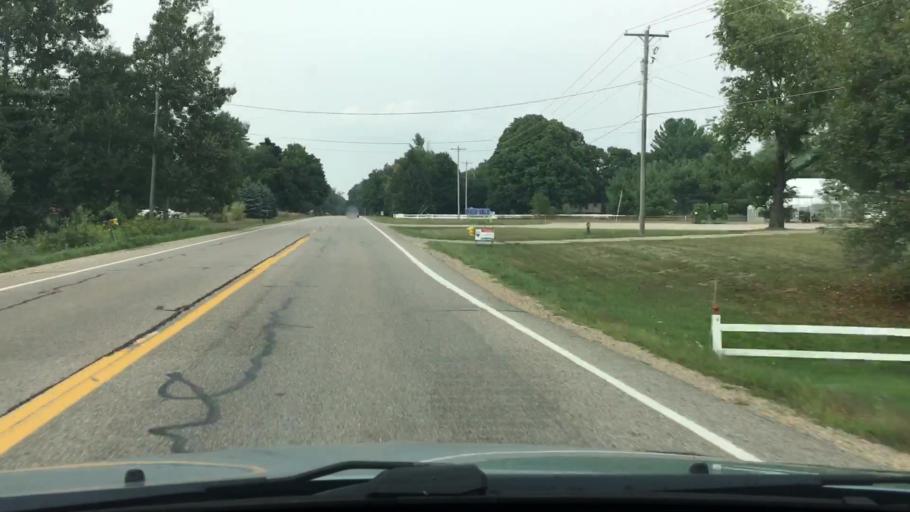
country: US
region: Michigan
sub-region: Ottawa County
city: Hudsonville
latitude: 42.8920
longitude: -85.9016
